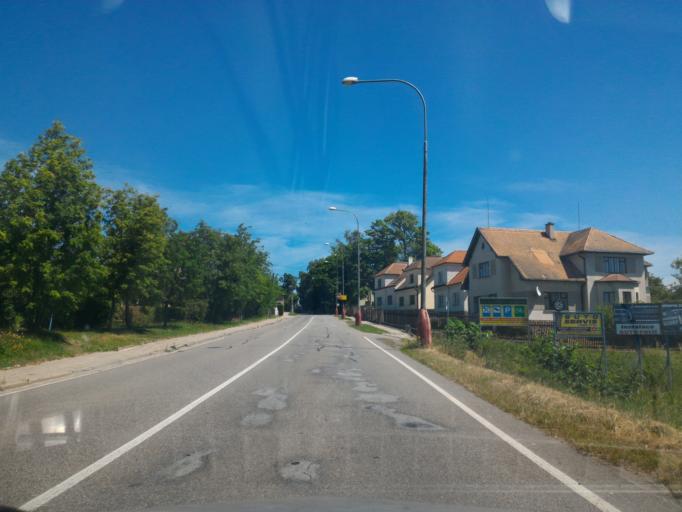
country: CZ
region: Vysocina
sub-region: Okres Jihlava
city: Trest'
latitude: 49.2835
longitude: 15.4793
